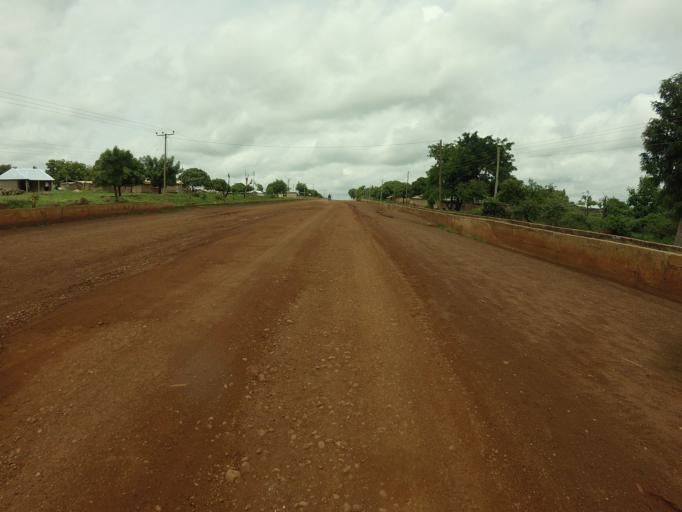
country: GH
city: Kpandae
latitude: 8.4550
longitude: 0.3448
